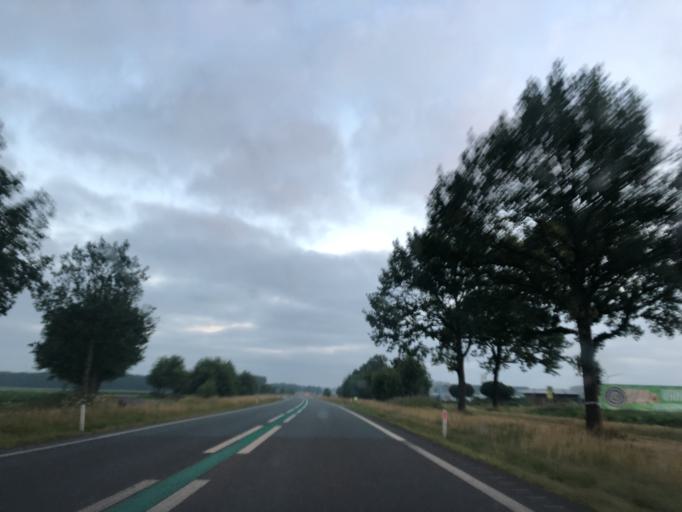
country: NL
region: Drenthe
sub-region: Gemeente Borger-Odoorn
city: Borger
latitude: 52.9922
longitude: 6.7606
